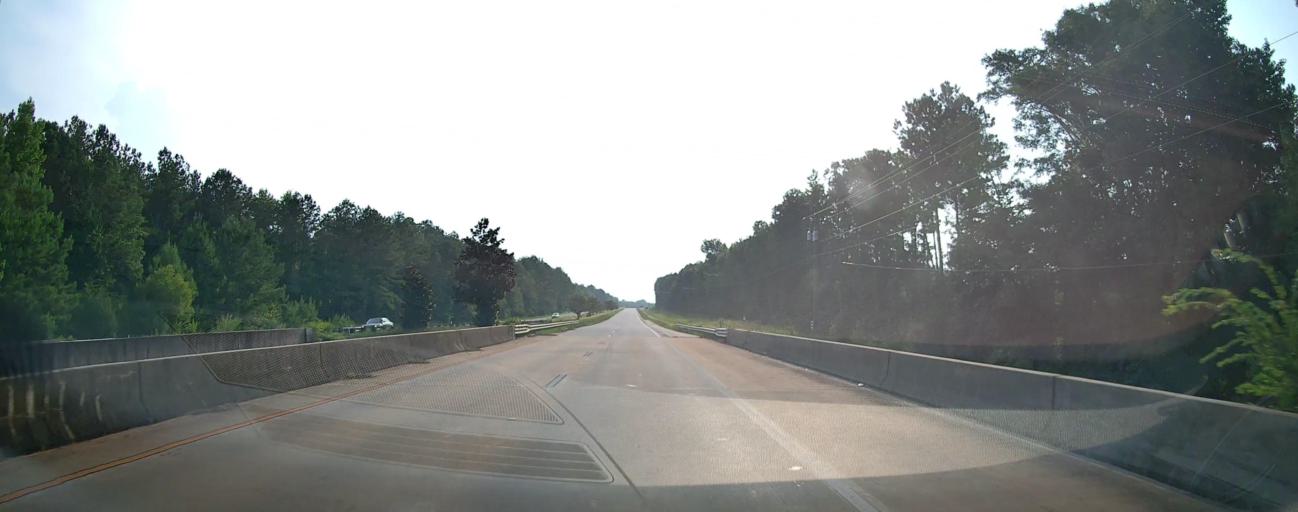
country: US
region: Georgia
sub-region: Talbot County
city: Talbotton
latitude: 32.5459
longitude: -84.7144
